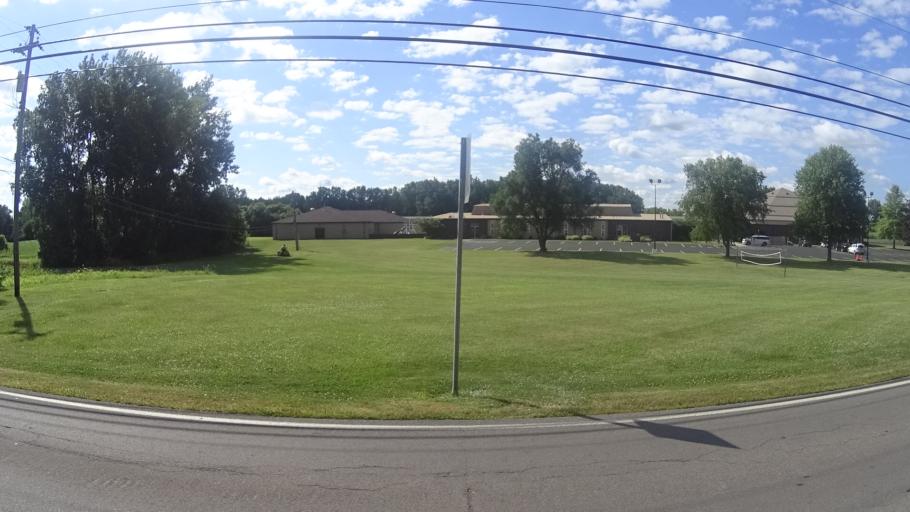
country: US
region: Ohio
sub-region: Erie County
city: Sandusky
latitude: 41.4266
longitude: -82.6686
